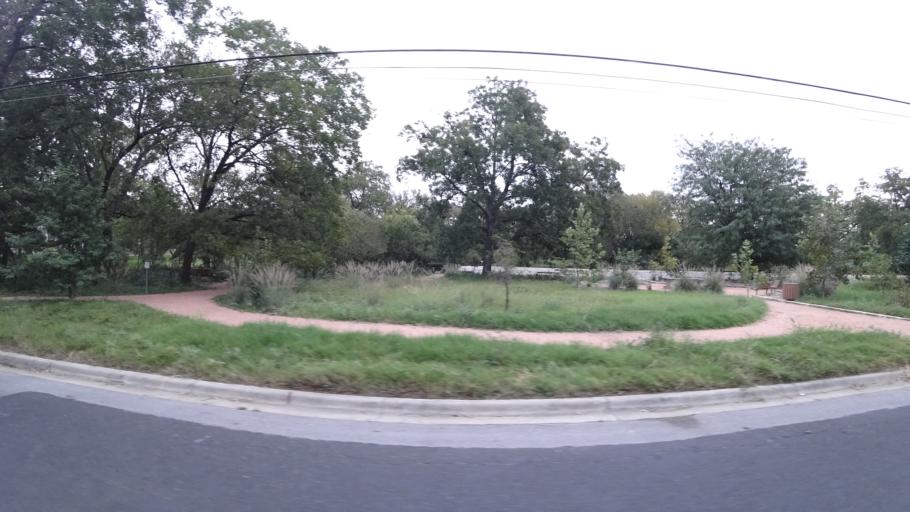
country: US
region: Texas
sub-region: Travis County
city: Austin
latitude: 30.2686
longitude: -97.7159
